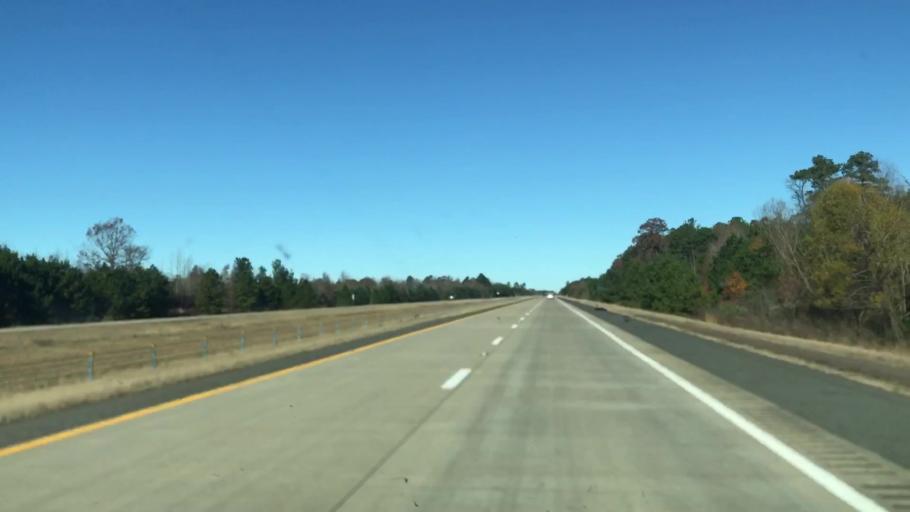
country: US
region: Texas
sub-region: Bowie County
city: Texarkana
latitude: 33.2990
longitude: -93.9278
